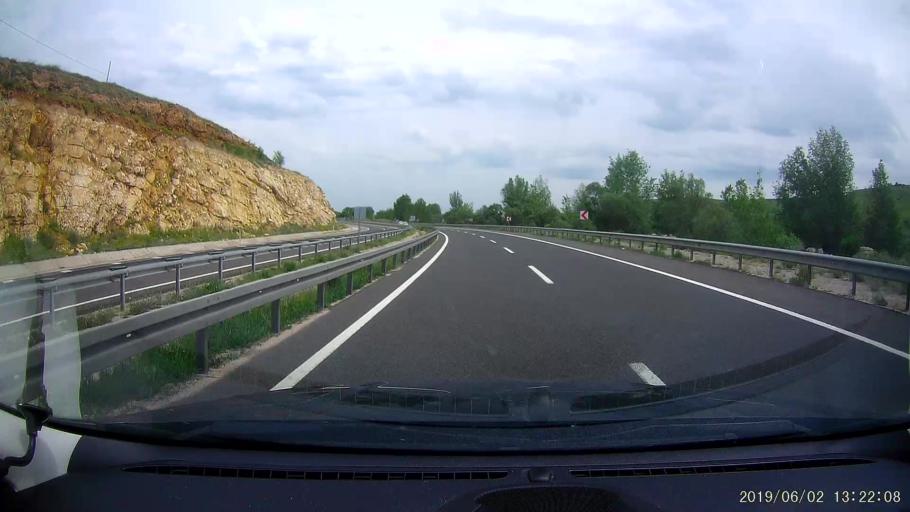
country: TR
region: Cankiri
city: Cerkes
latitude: 40.8261
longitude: 32.7909
